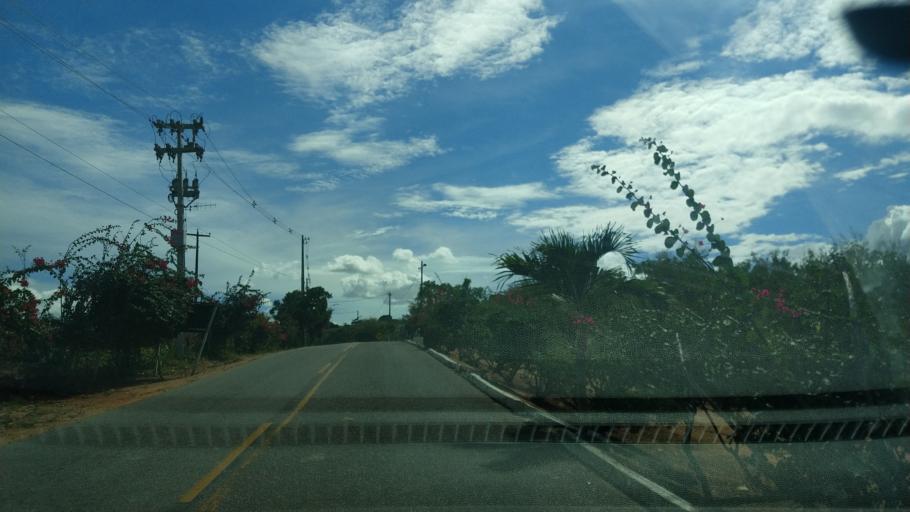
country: BR
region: Rio Grande do Norte
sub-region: Sao Jose Do Campestre
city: Sao Jose do Campestre
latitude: -6.4206
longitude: -35.7154
